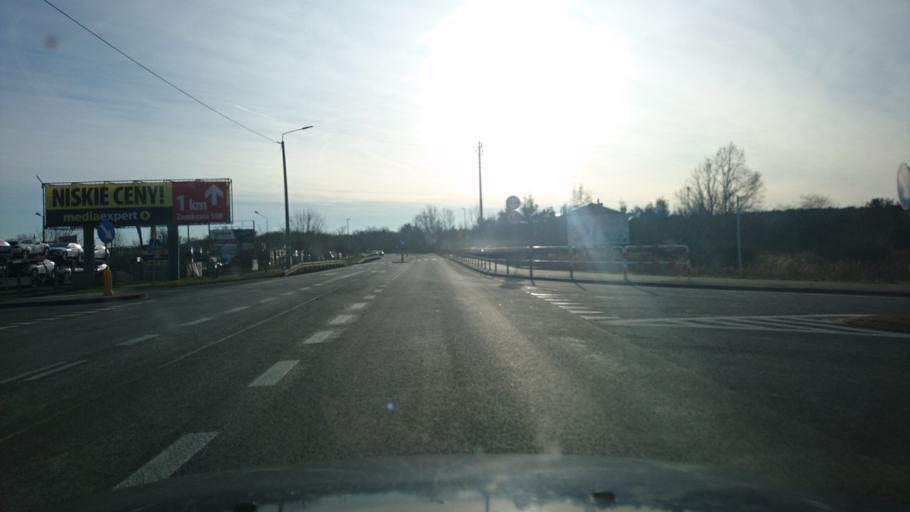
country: PL
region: Greater Poland Voivodeship
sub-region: Powiat ostrzeszowski
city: Ostrzeszow
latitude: 51.4367
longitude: 17.9151
